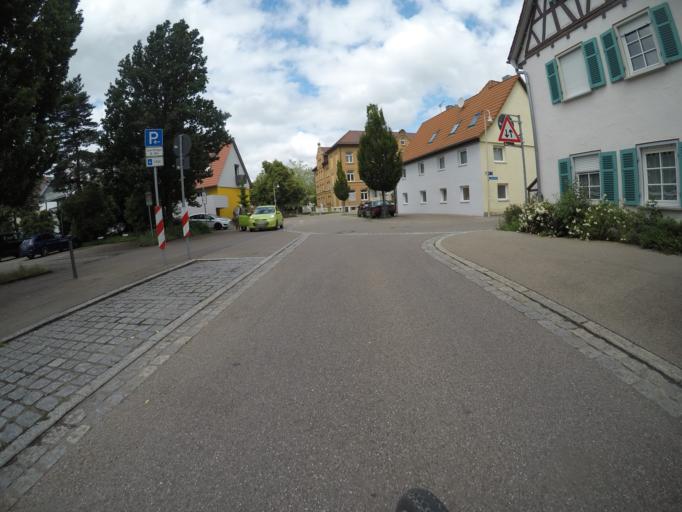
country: DE
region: Baden-Wuerttemberg
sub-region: Regierungsbezirk Stuttgart
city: Eislingen
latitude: 48.7008
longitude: 9.7070
